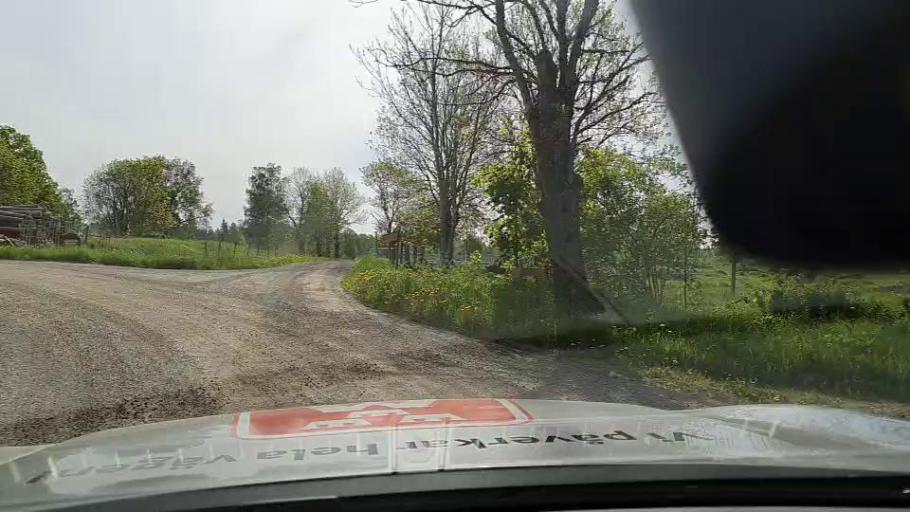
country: SE
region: Soedermanland
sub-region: Eskilstuna Kommun
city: Arla
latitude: 59.2584
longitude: 16.7930
